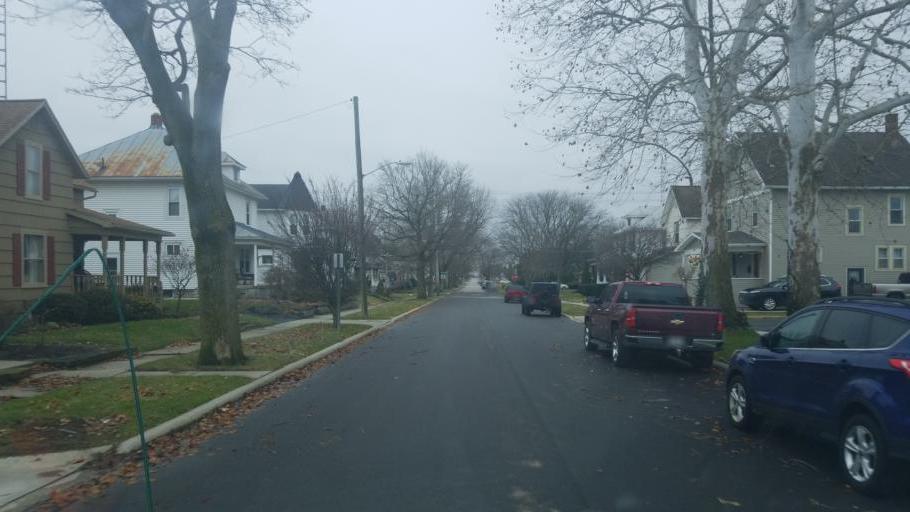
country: US
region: Ohio
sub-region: Crawford County
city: Bucyrus
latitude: 40.7983
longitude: -82.9740
